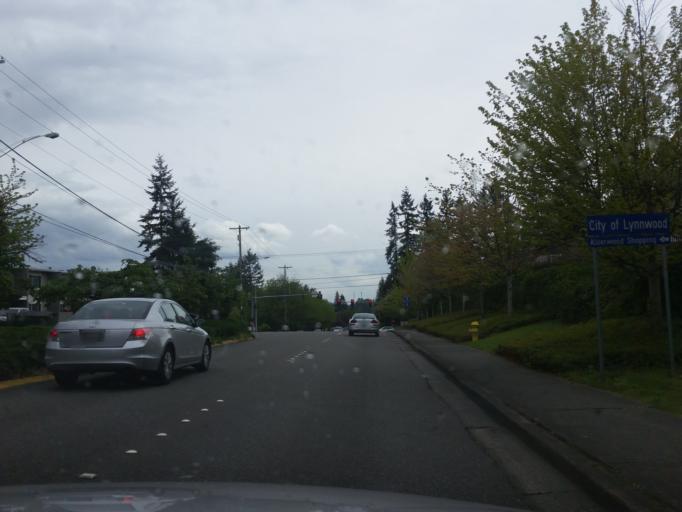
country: US
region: Washington
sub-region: Snohomish County
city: Alderwood Manor
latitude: 47.8294
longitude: -122.2819
